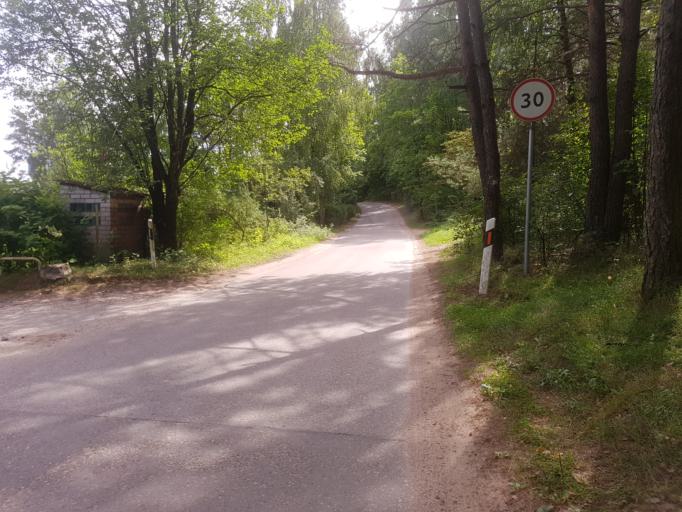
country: LT
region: Vilnius County
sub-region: Vilnius
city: Fabijoniskes
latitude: 54.7881
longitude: 25.3392
